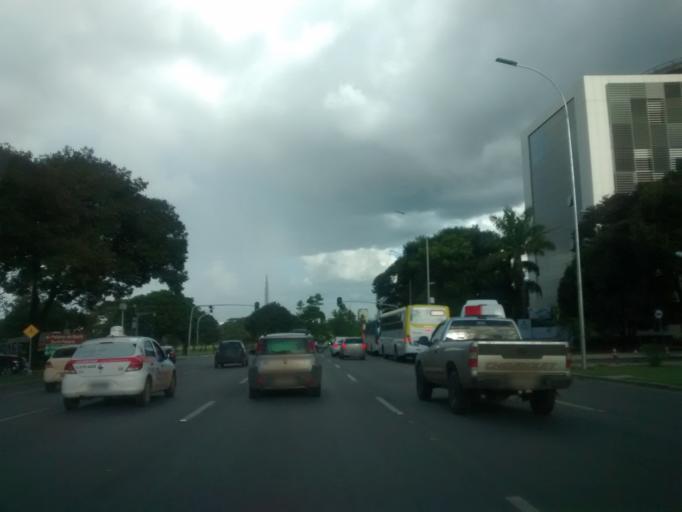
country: BR
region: Federal District
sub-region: Brasilia
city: Brasilia
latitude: -15.7867
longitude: -47.9086
